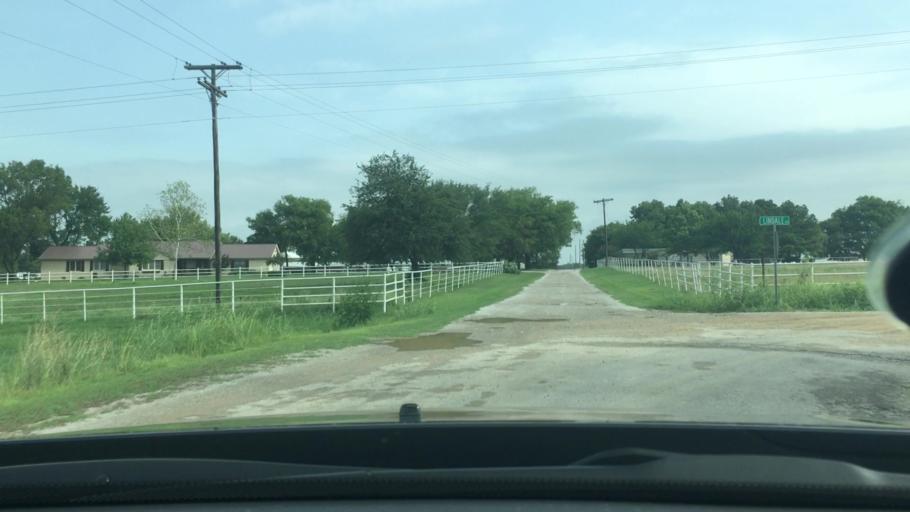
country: US
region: Oklahoma
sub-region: Carter County
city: Lone Grove
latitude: 34.2163
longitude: -97.2650
